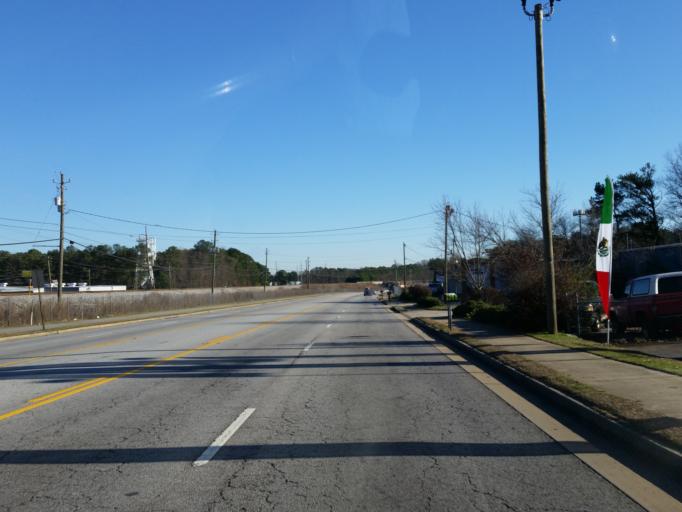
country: US
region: Georgia
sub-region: Cobb County
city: Fair Oaks
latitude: 33.9103
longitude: -84.5322
